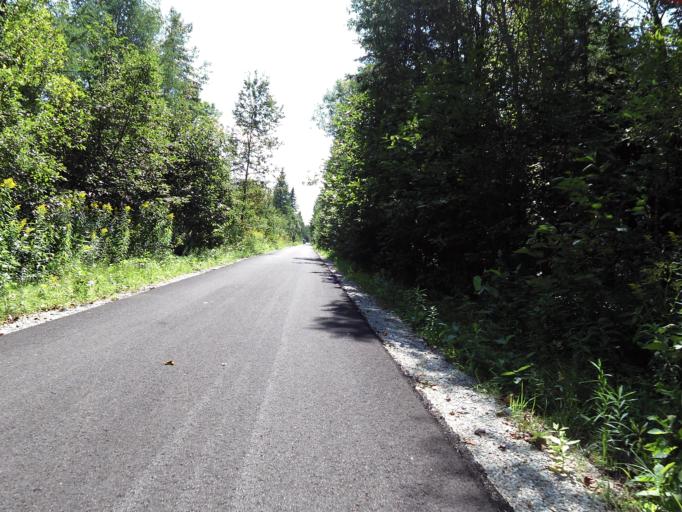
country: CA
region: Quebec
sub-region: Outaouais
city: Maniwaki
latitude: 46.1761
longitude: -76.0414
